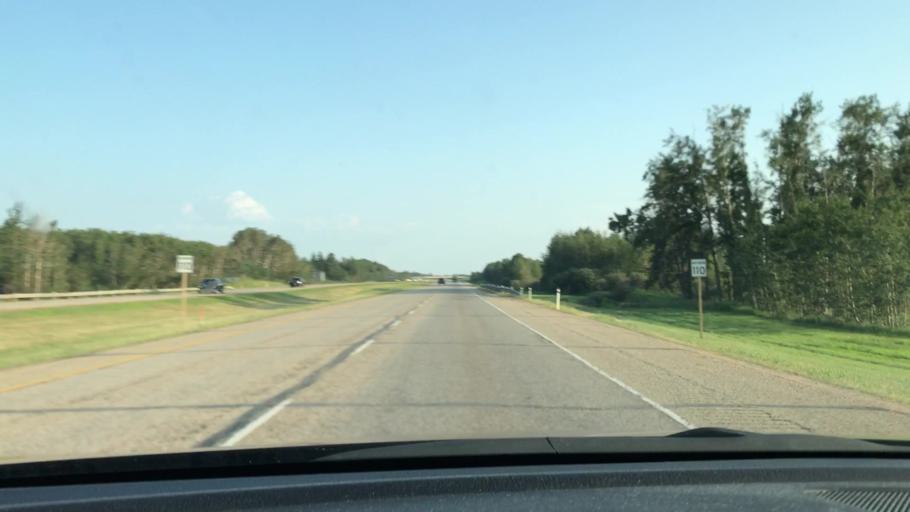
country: CA
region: Alberta
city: Lacombe
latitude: 52.5738
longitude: -113.6631
